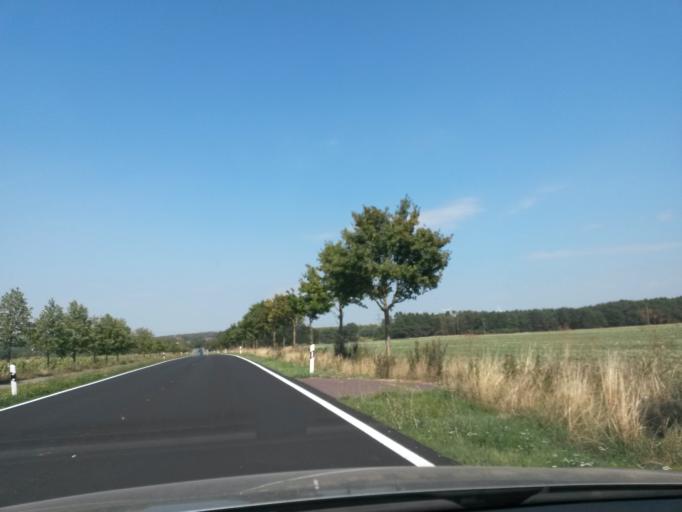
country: DE
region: Saxony-Anhalt
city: Jerichow
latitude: 52.4006
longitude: 11.9961
